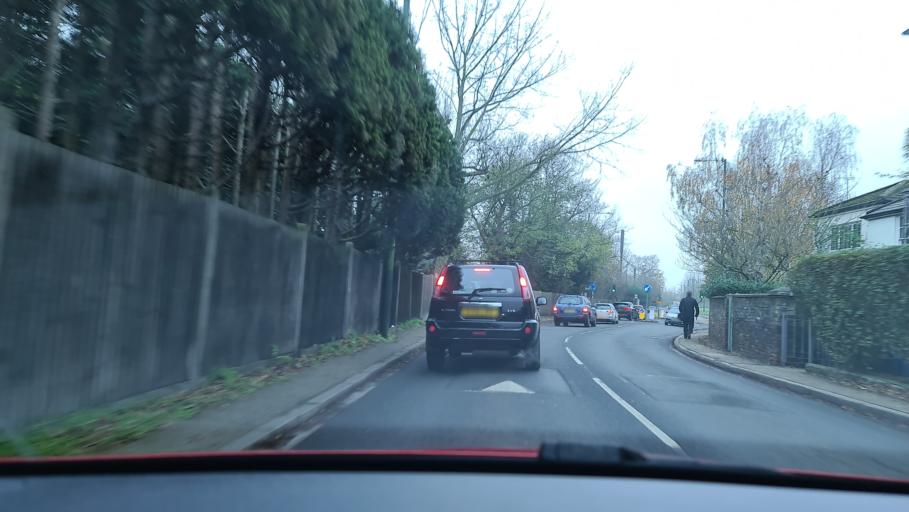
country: GB
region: England
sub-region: Greater London
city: Richmond
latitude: 51.4414
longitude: -0.3033
